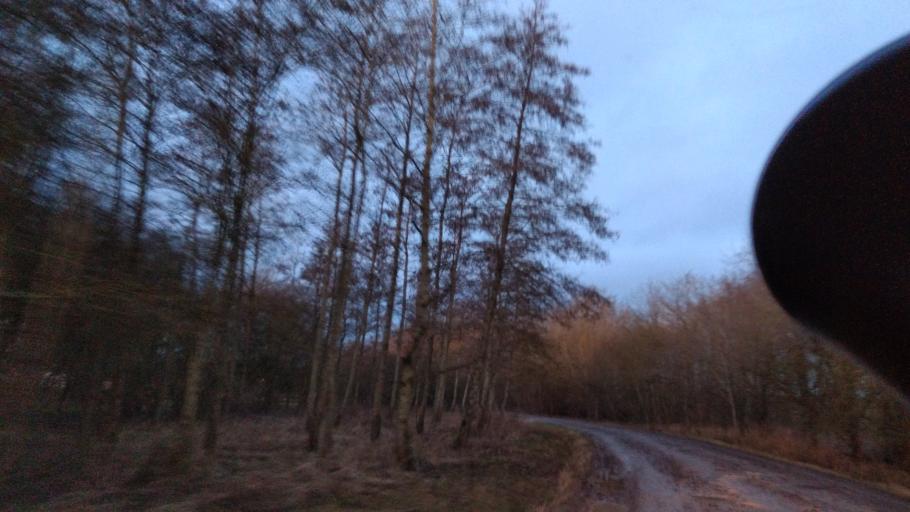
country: GB
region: England
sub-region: Borough of Swindon
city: Highworth
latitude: 51.5936
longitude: -1.7062
